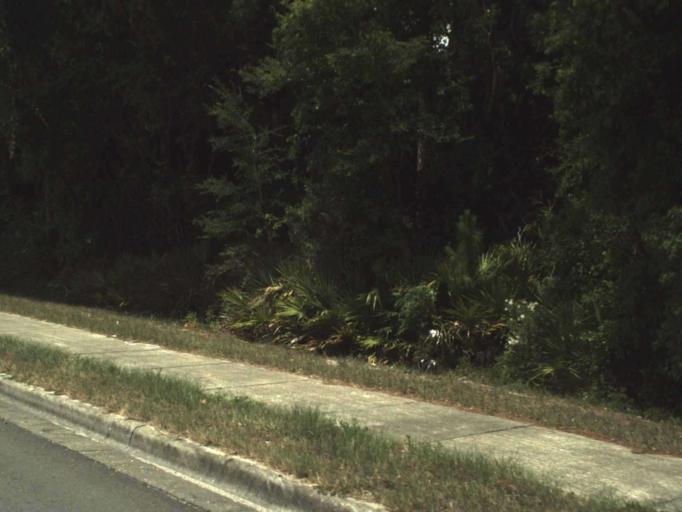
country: US
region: Florida
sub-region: Lake County
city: Leesburg
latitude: 28.8117
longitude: -81.9260
